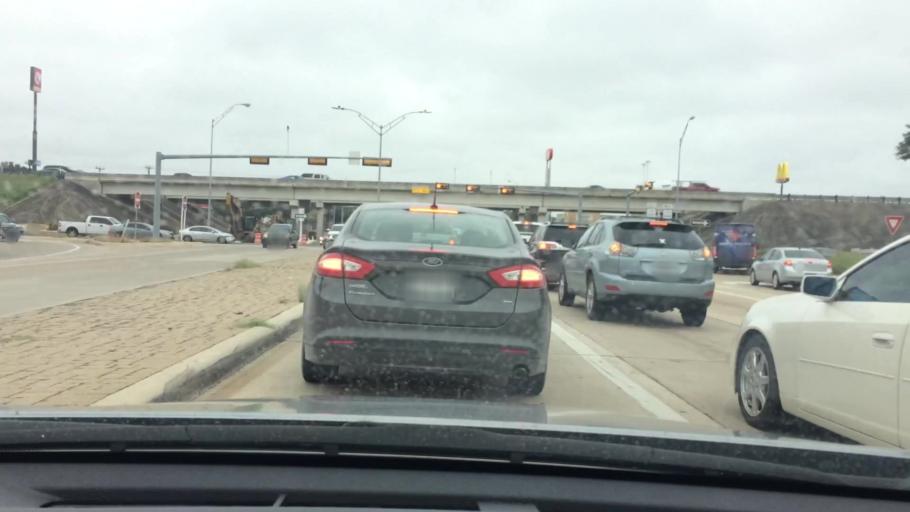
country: US
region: Texas
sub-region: Bexar County
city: Hollywood Park
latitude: 29.6019
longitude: -98.4185
